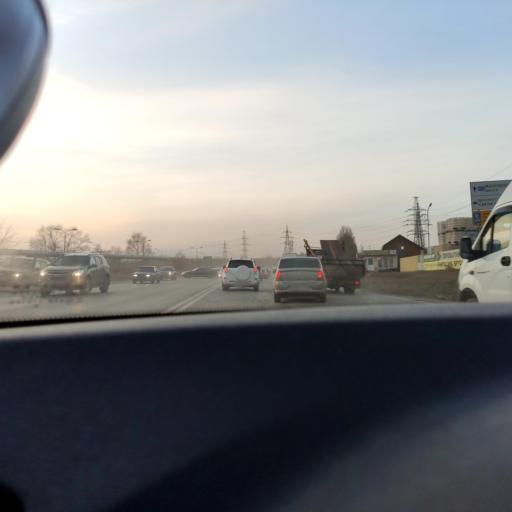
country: RU
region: Samara
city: Petra-Dubrava
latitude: 53.2578
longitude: 50.2950
